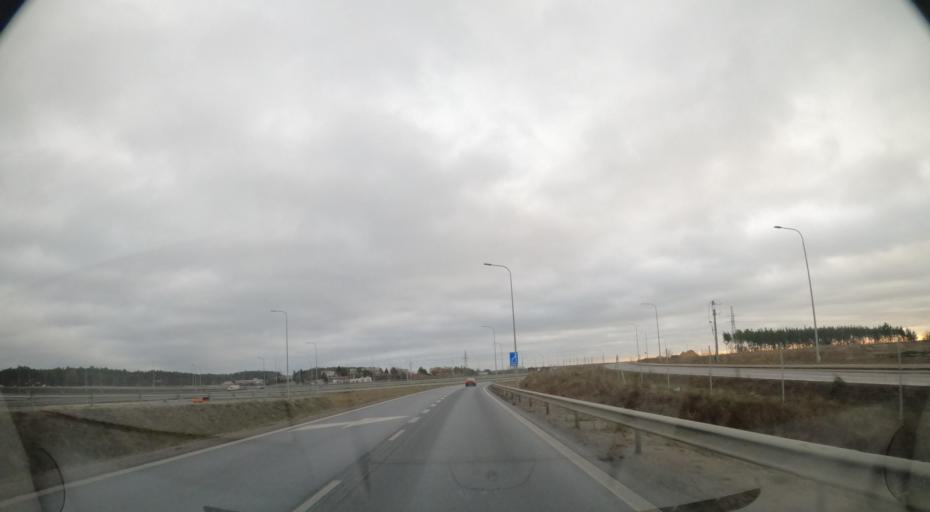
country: PL
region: Kujawsko-Pomorskie
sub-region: Powiat bydgoski
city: Biale Blota
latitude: 53.1559
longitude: 17.8836
